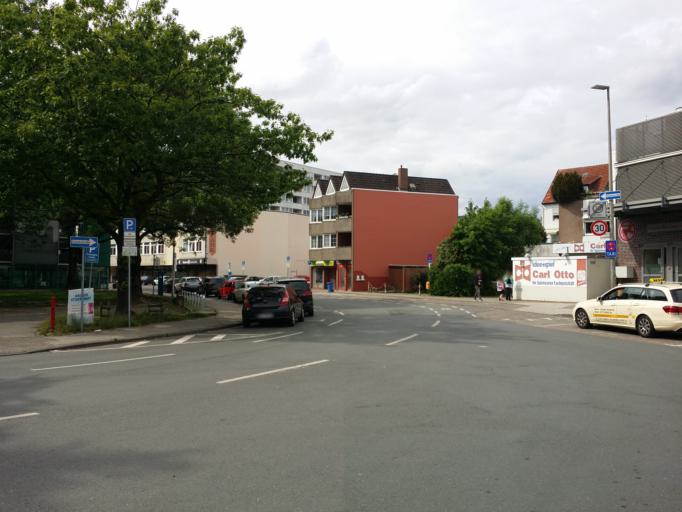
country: DE
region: Lower Saxony
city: Delmenhorst
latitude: 53.0487
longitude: 8.6281
